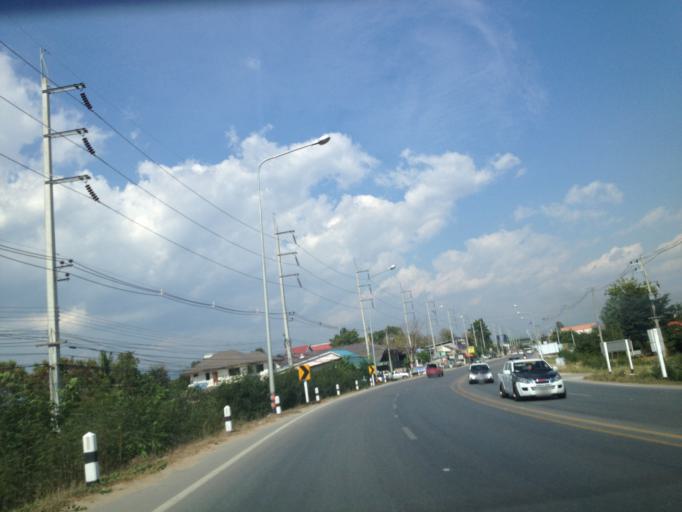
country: TH
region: Chiang Mai
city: Chom Thong
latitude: 18.4081
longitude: 98.6740
